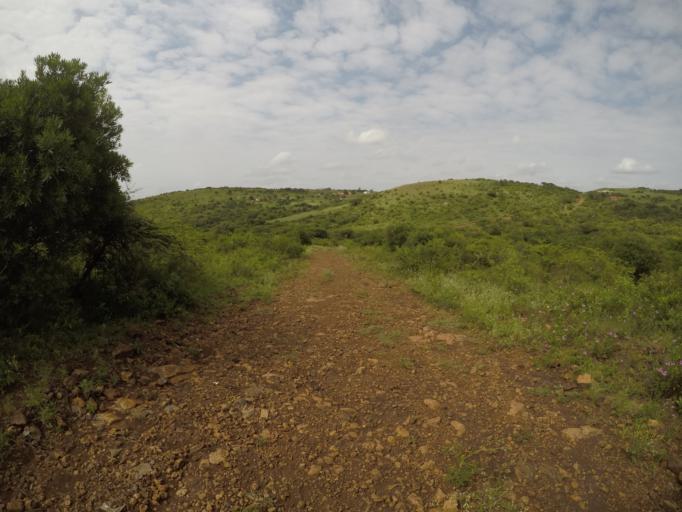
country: ZA
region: KwaZulu-Natal
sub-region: uThungulu District Municipality
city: Empangeni
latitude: -28.6131
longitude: 31.9048
